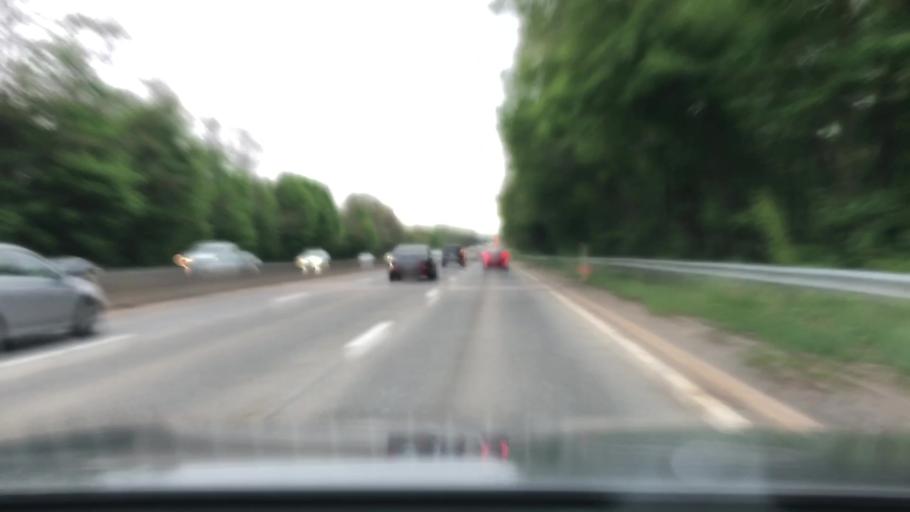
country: US
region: New York
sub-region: Nassau County
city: Uniondale
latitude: 40.7115
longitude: -73.5798
